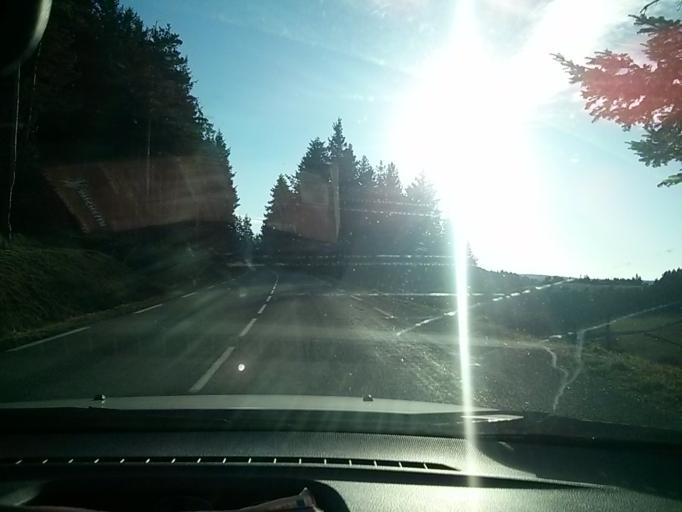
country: FR
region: Rhone-Alpes
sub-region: Departement de la Loire
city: Saint-Genest-Malifaux
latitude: 45.3839
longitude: 4.4819
